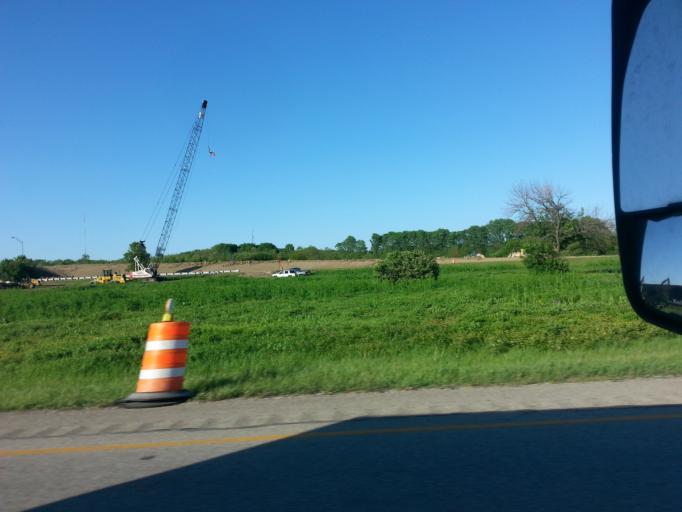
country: US
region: Illinois
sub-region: McLean County
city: Bloomington
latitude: 40.4399
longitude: -89.0185
